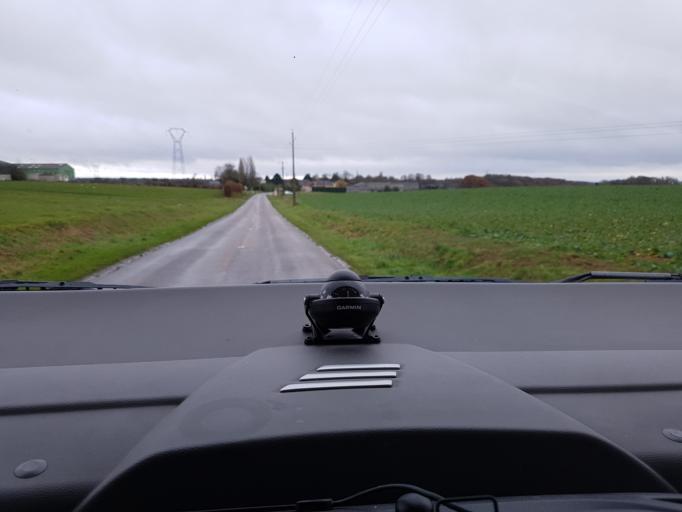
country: FR
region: Haute-Normandie
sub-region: Departement de l'Eure
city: Fleury-sur-Andelle
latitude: 49.2945
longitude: 1.3349
